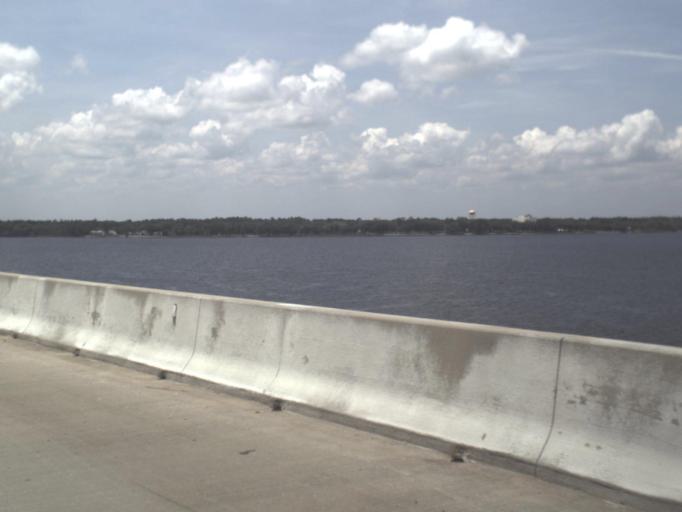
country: US
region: Florida
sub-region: Clay County
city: Orange Park
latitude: 30.1902
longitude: -81.6672
